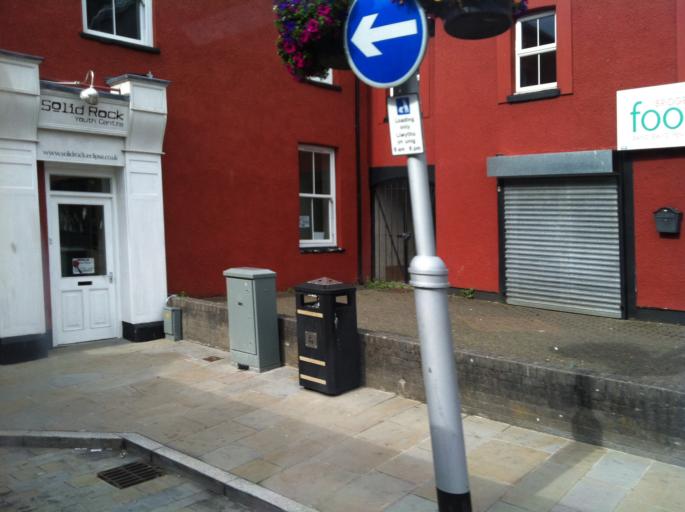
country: GB
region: Wales
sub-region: Bridgend county borough
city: Bridgend
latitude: 51.5026
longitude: -3.5763
